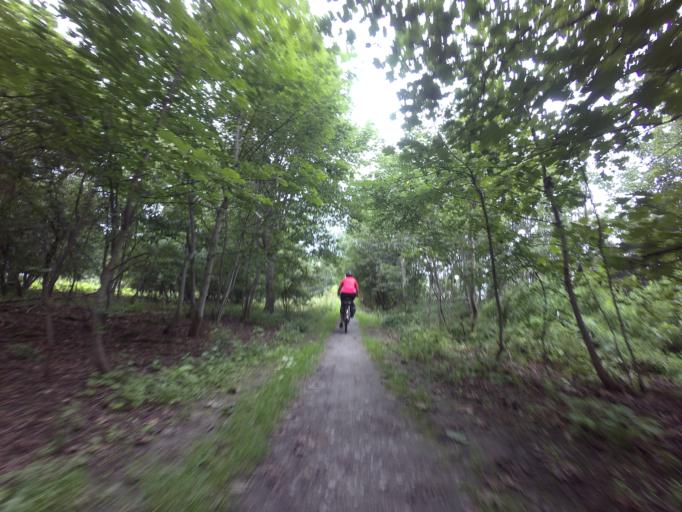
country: GB
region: Scotland
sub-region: Moray
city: Forres
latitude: 57.6148
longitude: -3.6315
